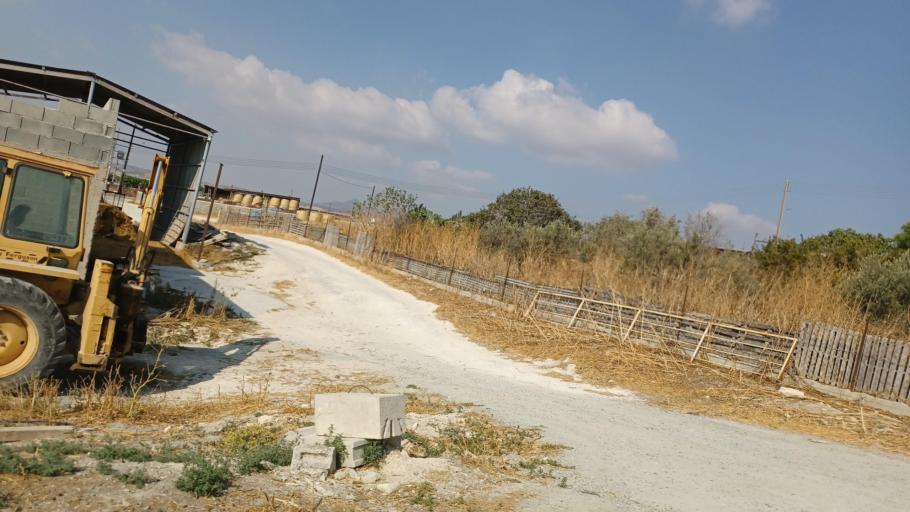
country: CY
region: Larnaka
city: Psevdas
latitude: 34.9381
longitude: 33.5274
